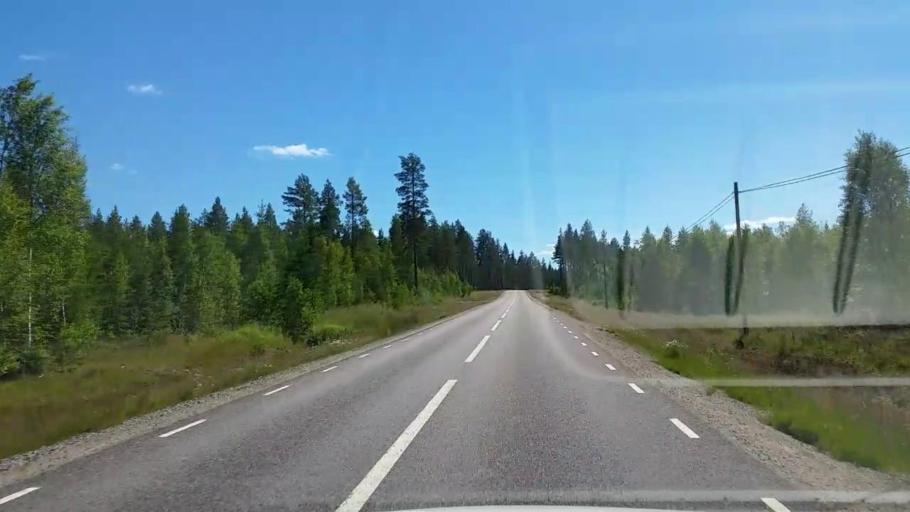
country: SE
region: Gaevleborg
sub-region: Ovanakers Kommun
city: Edsbyn
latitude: 61.4500
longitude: 15.7096
